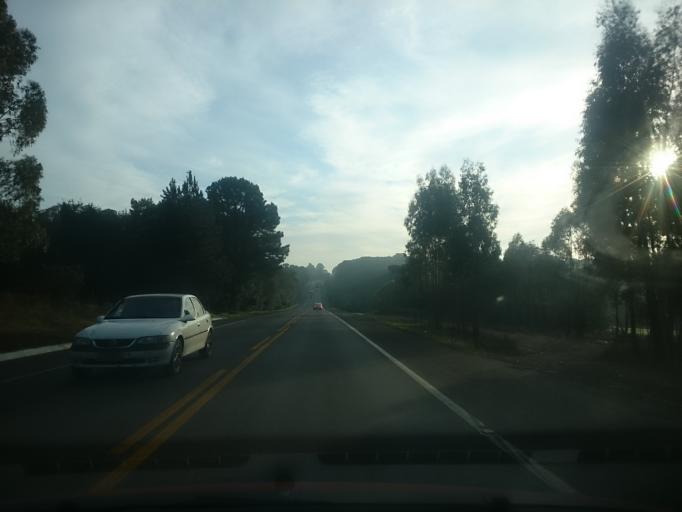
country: BR
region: Rio Grande do Sul
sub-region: Vacaria
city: Estrela
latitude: -28.2763
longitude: -50.7973
